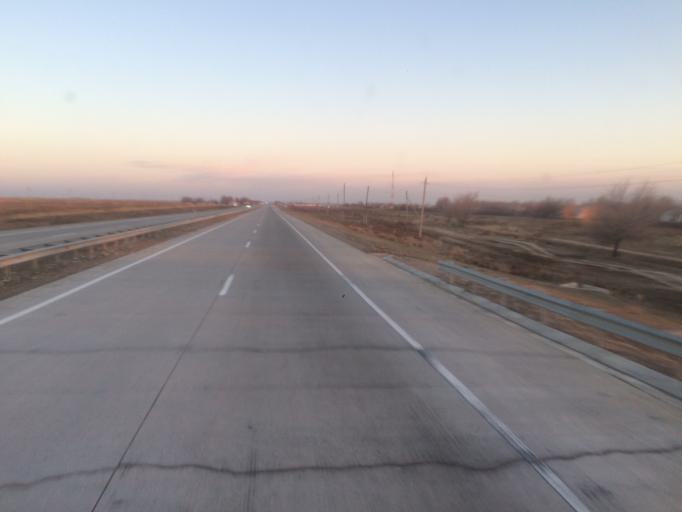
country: KZ
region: Ongtustik Qazaqstan
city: Bayaldyr
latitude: 43.0657
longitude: 68.6749
